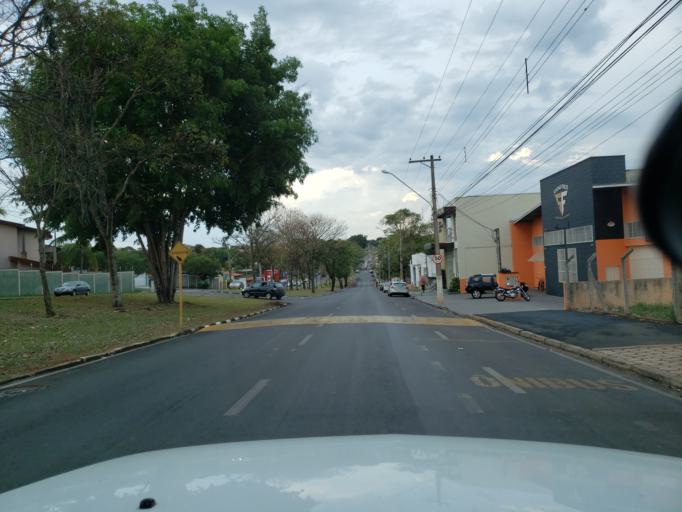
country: BR
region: Sao Paulo
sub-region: Moji-Guacu
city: Mogi-Gaucu
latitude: -22.3613
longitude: -46.9399
